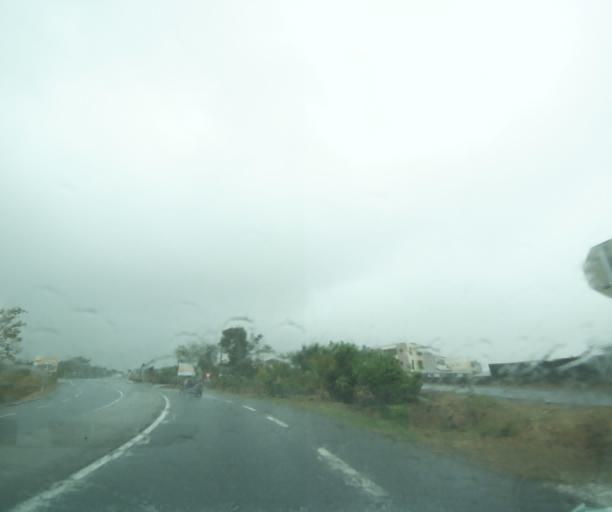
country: RE
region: Reunion
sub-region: Reunion
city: Saint-Paul
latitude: -21.0175
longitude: 55.2654
